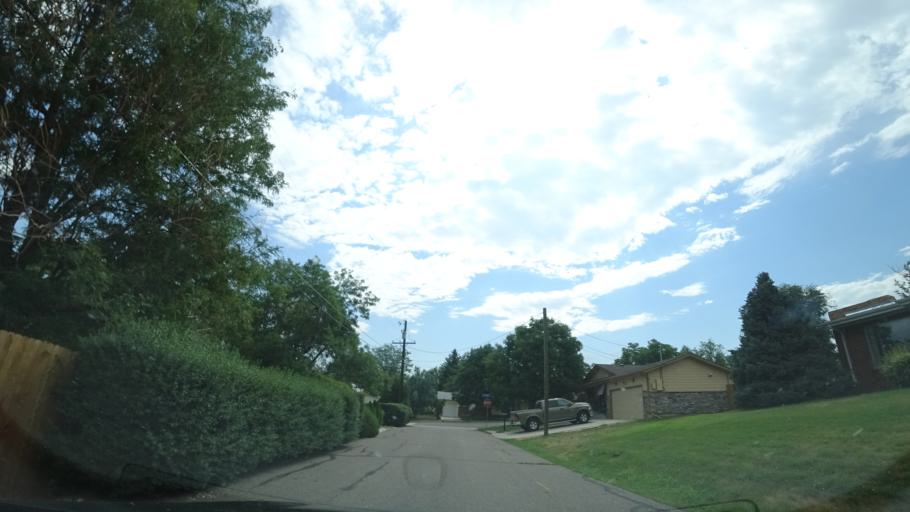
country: US
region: Colorado
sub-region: Jefferson County
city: Lakewood
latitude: 39.7240
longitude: -105.0646
